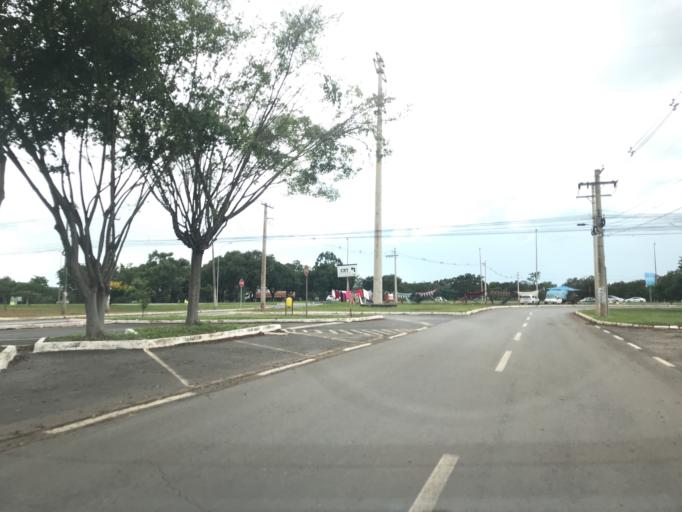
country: BR
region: Federal District
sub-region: Brasilia
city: Brasilia
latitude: -15.8232
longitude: -47.9519
